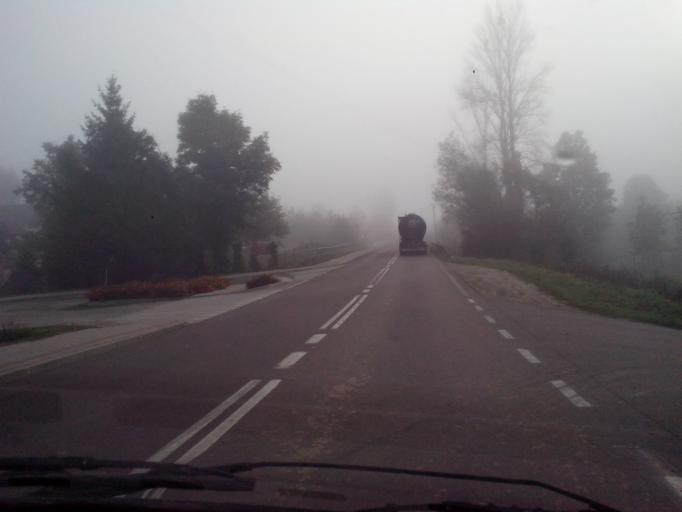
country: PL
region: Subcarpathian Voivodeship
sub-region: Powiat przemyski
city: Krasiczyn
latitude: 49.8074
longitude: 22.6678
